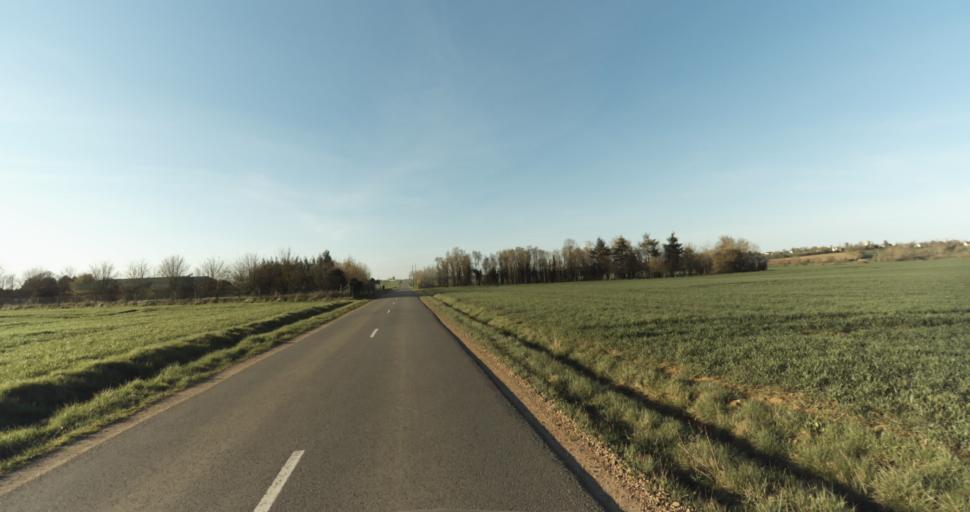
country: FR
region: Lower Normandy
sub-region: Departement du Calvados
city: Saint-Pierre-sur-Dives
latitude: 48.9965
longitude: -0.0207
